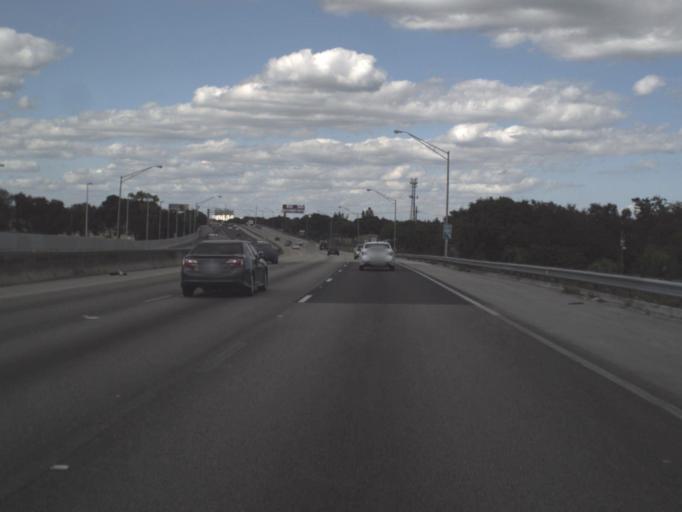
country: US
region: Florida
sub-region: Broward County
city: Pembroke Pines
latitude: 26.0110
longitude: -80.2129
